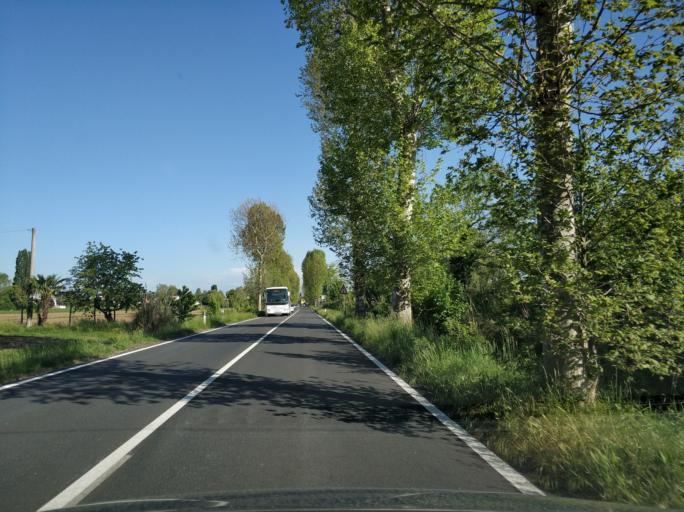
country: IT
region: Friuli Venezia Giulia
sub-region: Provincia di Udine
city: Terzo d'Aquileia
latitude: 45.7947
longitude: 13.3540
